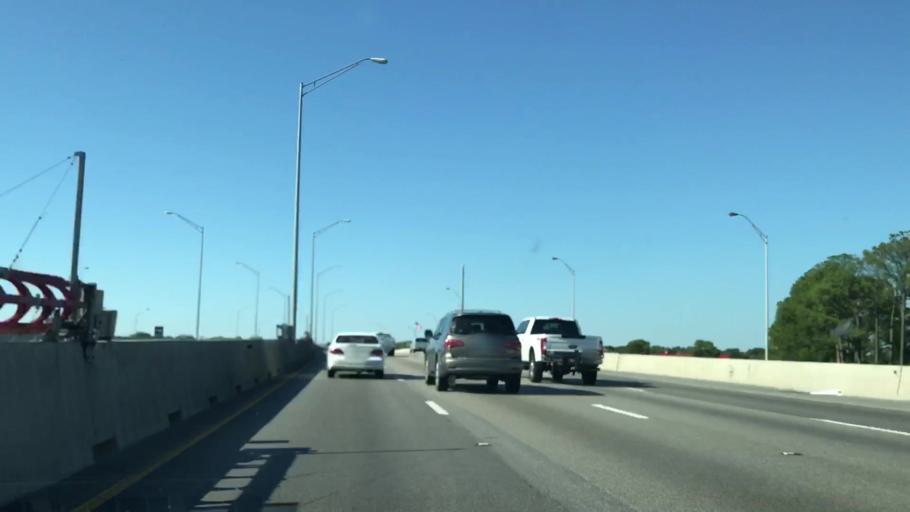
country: US
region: Texas
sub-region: Denton County
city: Lewisville
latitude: 33.0292
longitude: -96.9917
